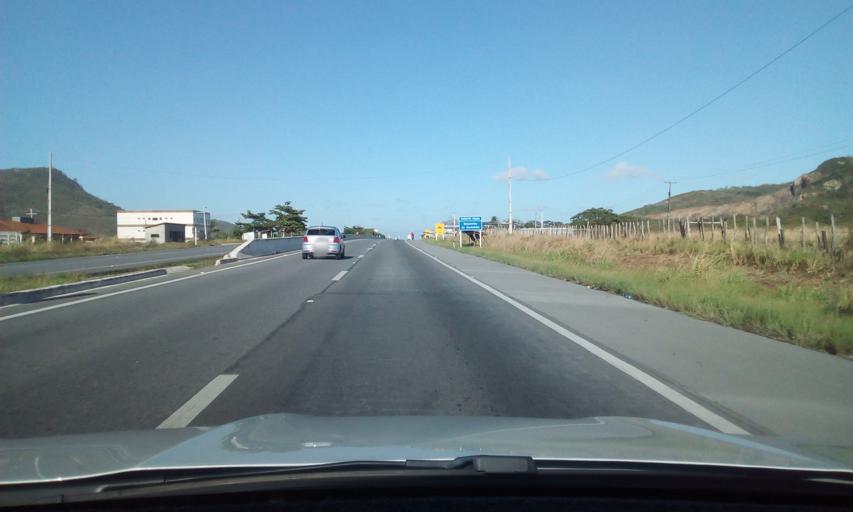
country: BR
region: Paraiba
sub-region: Gurinhem
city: Gurinhem
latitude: -7.1720
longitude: -35.3889
